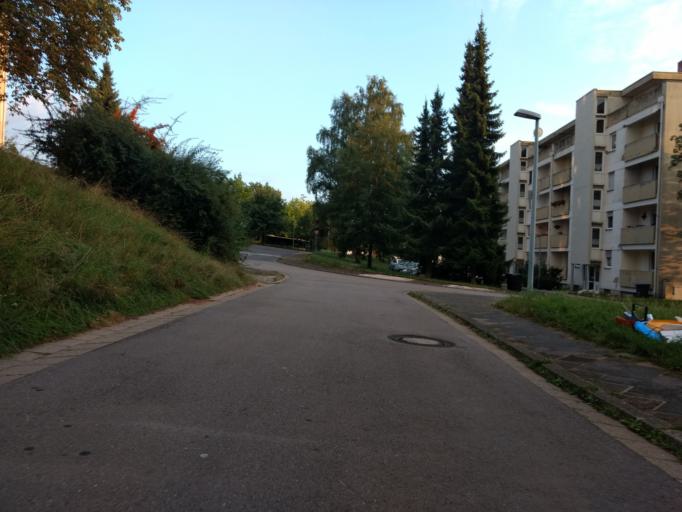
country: DE
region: Saarland
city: Dillingen
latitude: 49.3657
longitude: 6.7175
